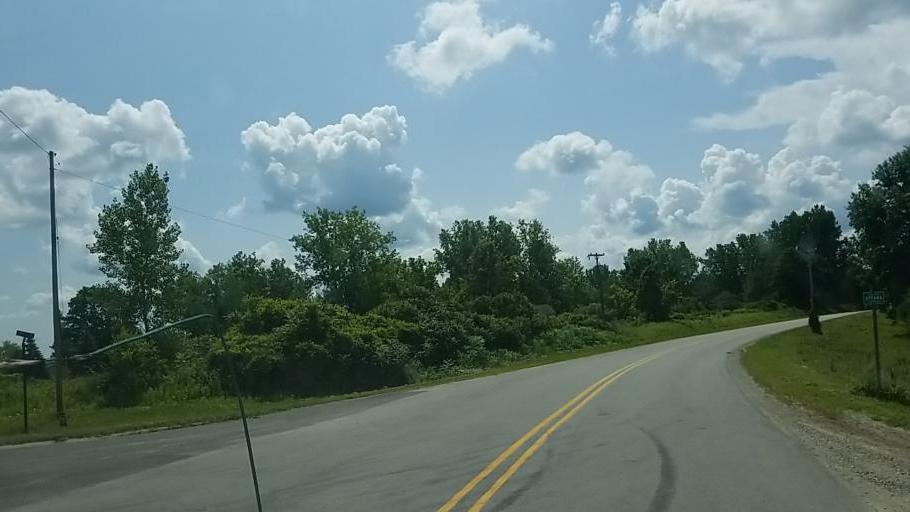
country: US
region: Michigan
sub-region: Muskegon County
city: Ravenna
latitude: 43.2059
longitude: -85.8796
